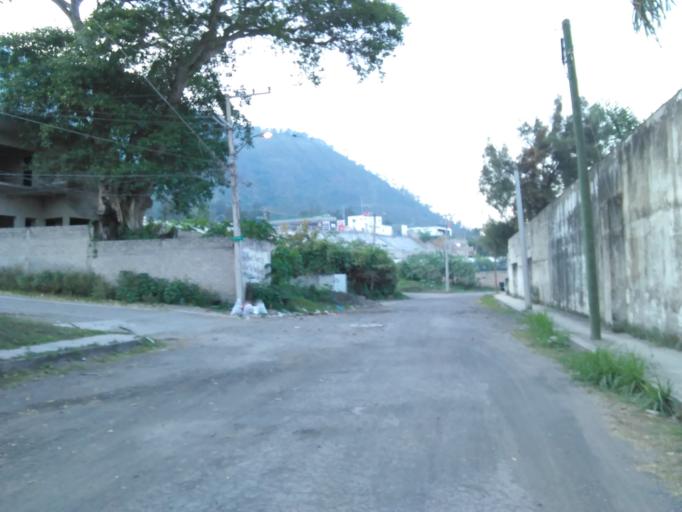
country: MX
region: Nayarit
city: Tepic
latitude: 21.5039
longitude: -104.9186
